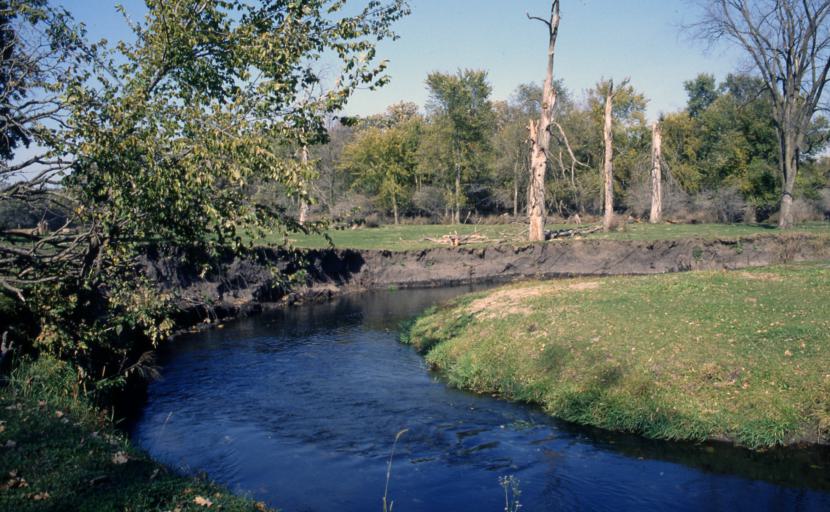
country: US
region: Minnesota
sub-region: Wabasha County
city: Elgin
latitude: 44.1221
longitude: -92.2029
